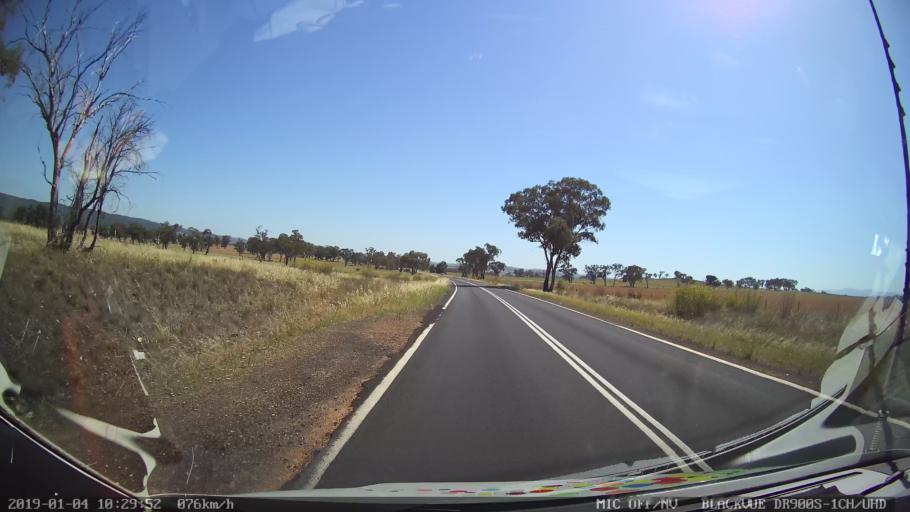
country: AU
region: New South Wales
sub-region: Cabonne
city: Canowindra
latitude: -33.3521
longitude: 148.6242
